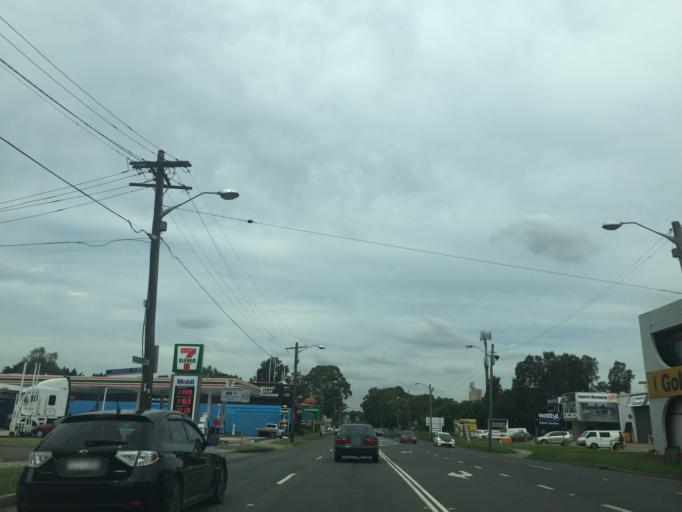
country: AU
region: New South Wales
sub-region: Parramatta
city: Granville
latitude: -33.8348
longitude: 151.0216
